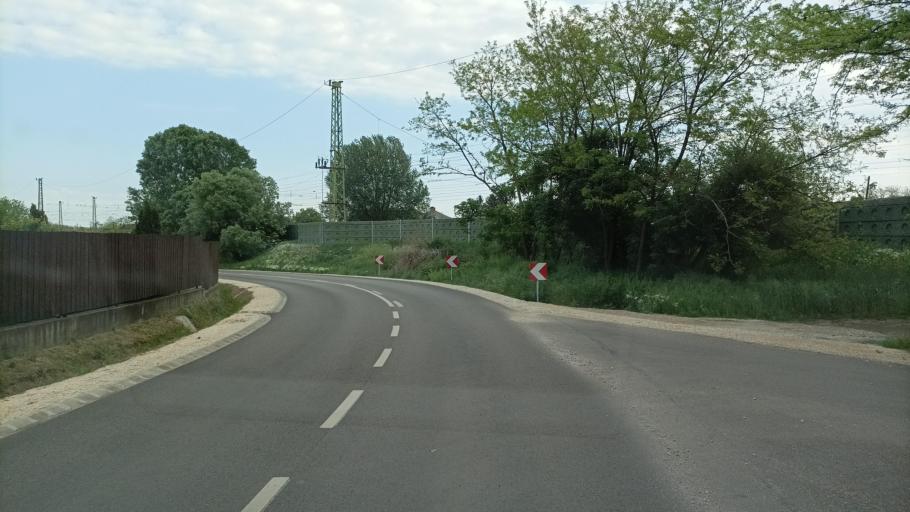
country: HU
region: Pest
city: Pilis
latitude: 47.2817
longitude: 19.5335
